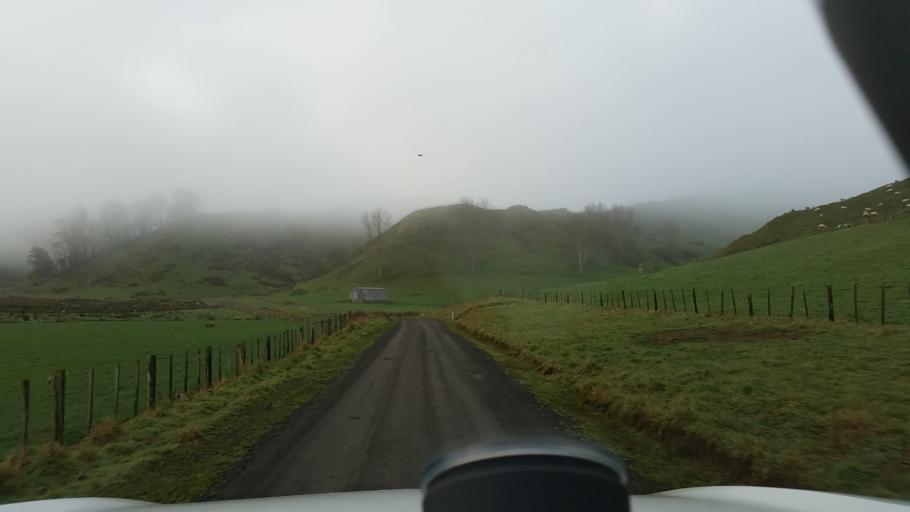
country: NZ
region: Taranaki
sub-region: South Taranaki District
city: Eltham
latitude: -39.4294
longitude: 174.4400
